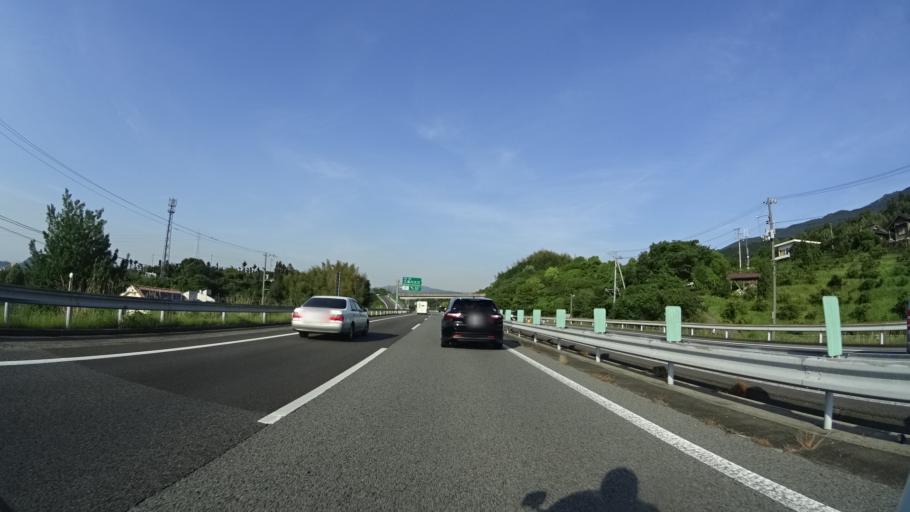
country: JP
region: Ehime
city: Kawanoecho
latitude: 33.9763
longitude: 133.5707
